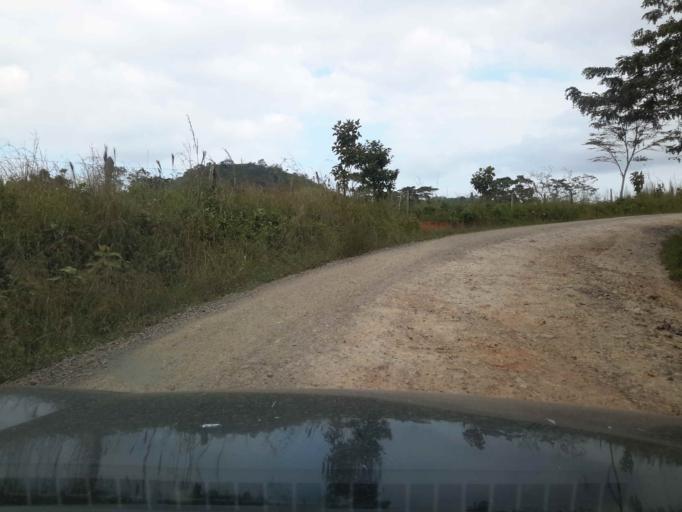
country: CR
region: Alajuela
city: Los Chiles
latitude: 11.1124
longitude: -84.5899
